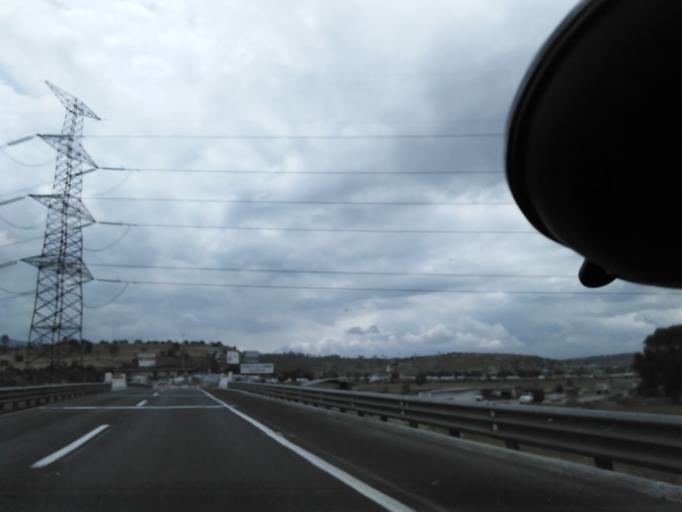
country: MX
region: Mexico
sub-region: Huehuetoca
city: Jorobas
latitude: 19.8217
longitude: -99.2374
